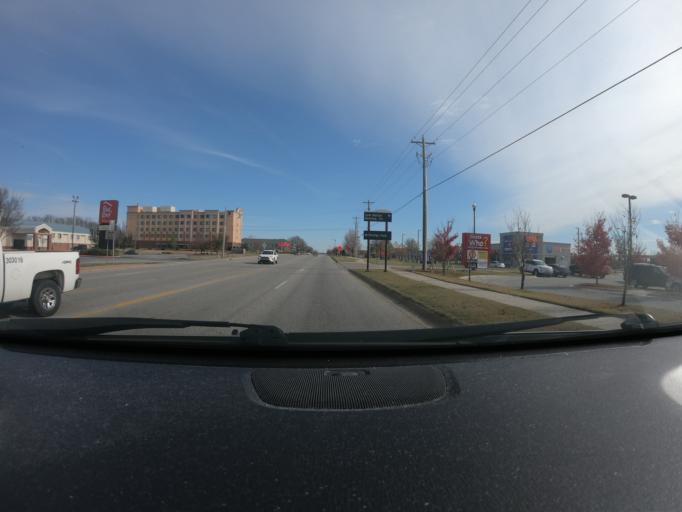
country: US
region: Arkansas
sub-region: Benton County
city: Bentonville
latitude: 36.3355
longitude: -94.2084
